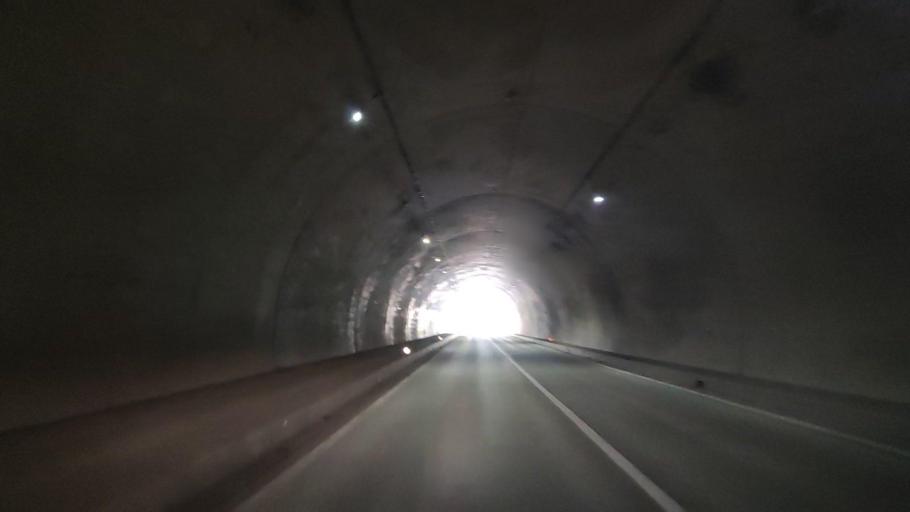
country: JP
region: Gifu
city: Takayama
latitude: 36.3358
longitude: 137.3010
